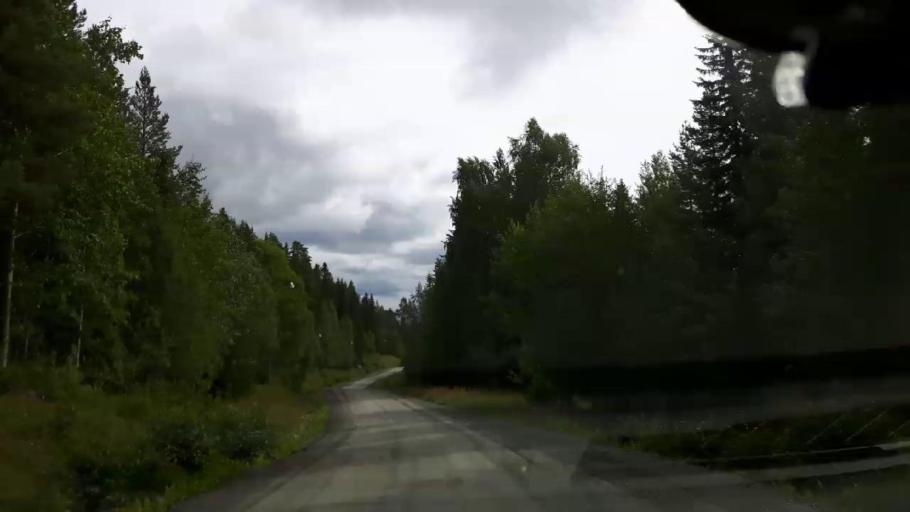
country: SE
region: Jaemtland
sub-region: Krokoms Kommun
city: Valla
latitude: 63.6211
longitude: 14.0589
